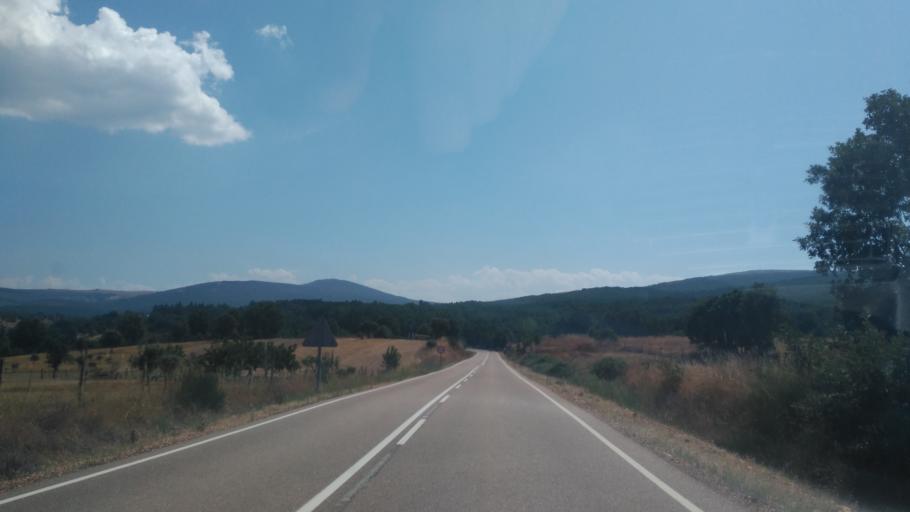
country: ES
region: Castille and Leon
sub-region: Provincia de Salamanca
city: Cereceda de la Sierra
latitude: 40.5678
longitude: -6.1154
